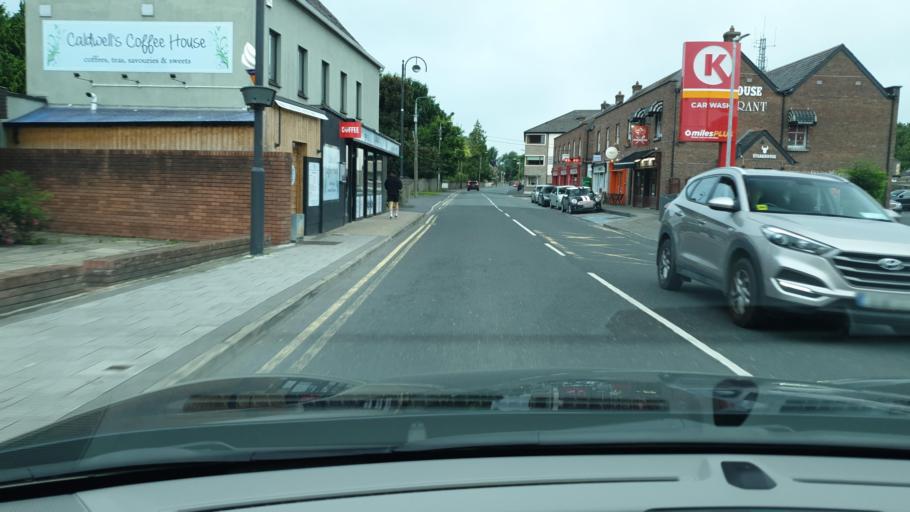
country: IE
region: Leinster
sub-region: An Mhi
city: Dunboyne
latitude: 53.4199
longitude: -6.4765
